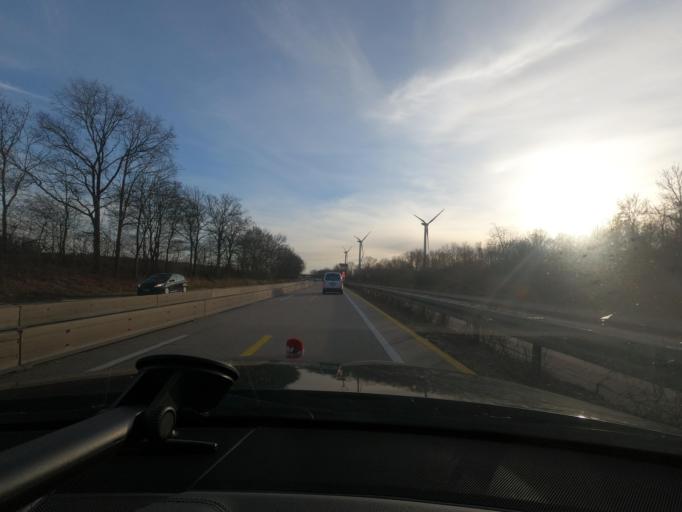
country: DE
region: Lower Saxony
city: Harsum
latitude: 52.2090
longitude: 9.9349
